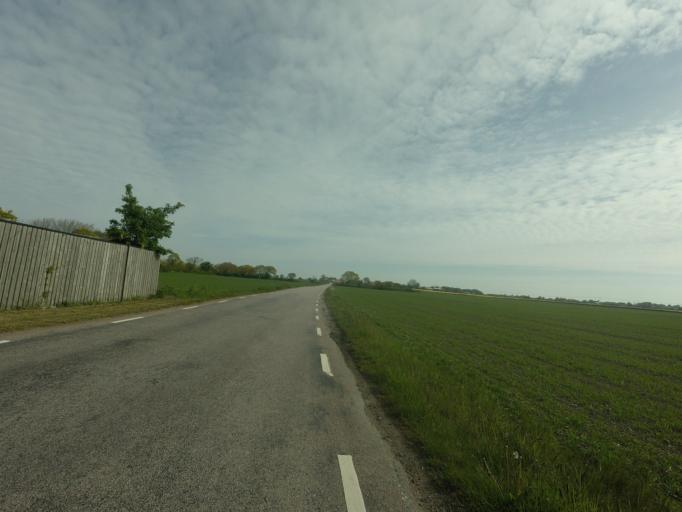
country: SE
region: Skane
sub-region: Hoganas Kommun
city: Hoganas
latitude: 56.2052
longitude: 12.5773
